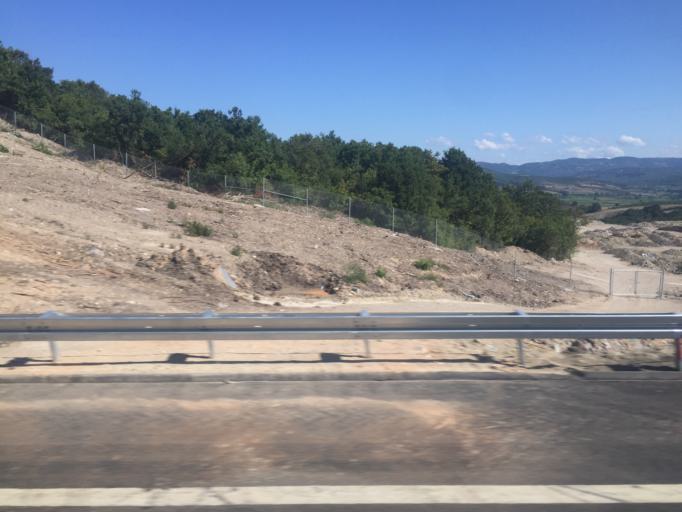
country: TR
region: Bursa
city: Mahmudiye
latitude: 40.2570
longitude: 28.7246
